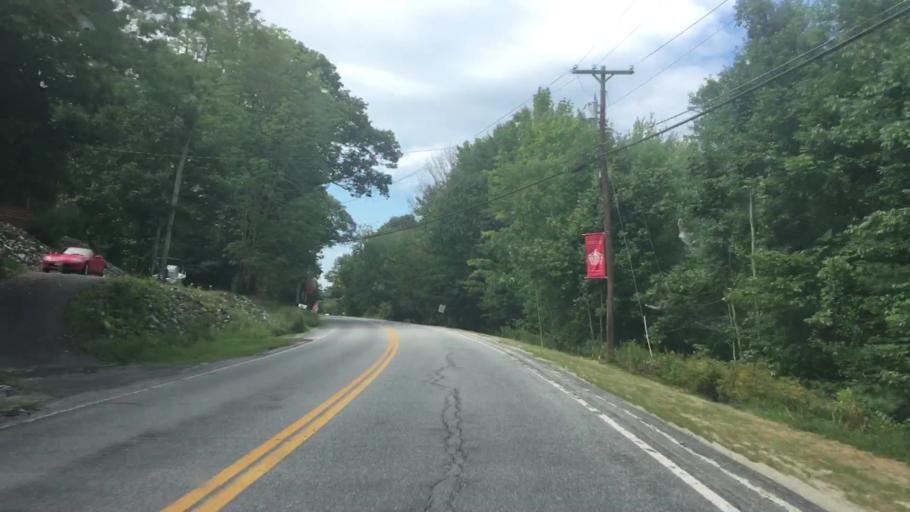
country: US
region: Maine
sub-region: Cumberland County
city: Raymond
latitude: 44.0004
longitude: -70.5195
